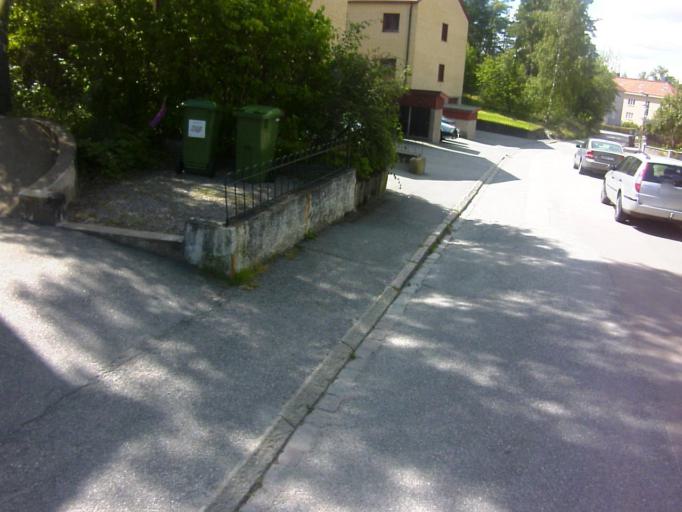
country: SE
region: Soedermanland
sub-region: Eskilstuna Kommun
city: Eskilstuna
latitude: 59.3596
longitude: 16.5008
